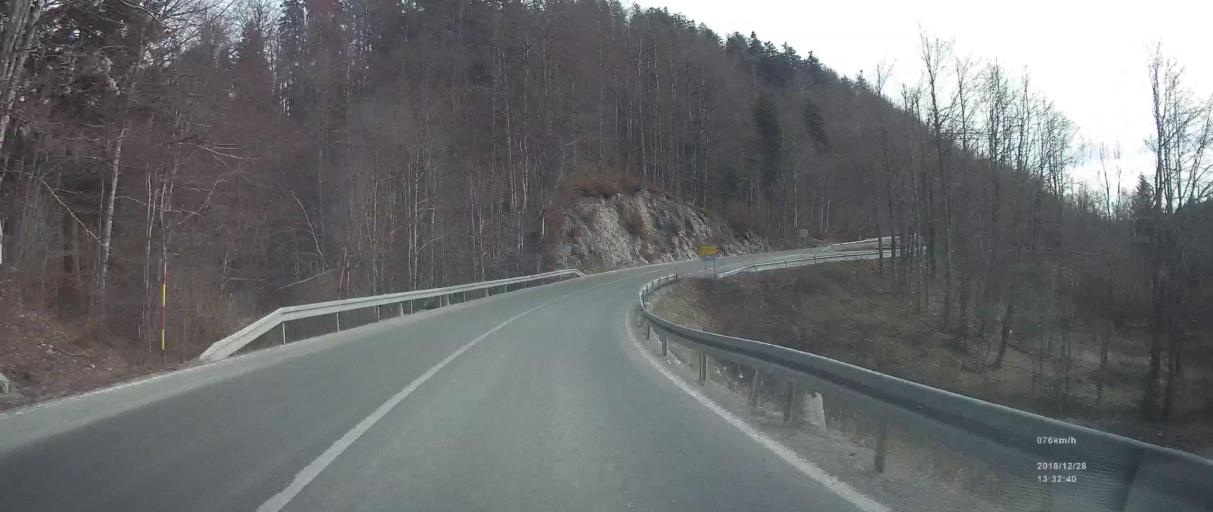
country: HR
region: Primorsko-Goranska
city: Hreljin
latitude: 45.3450
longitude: 14.6680
